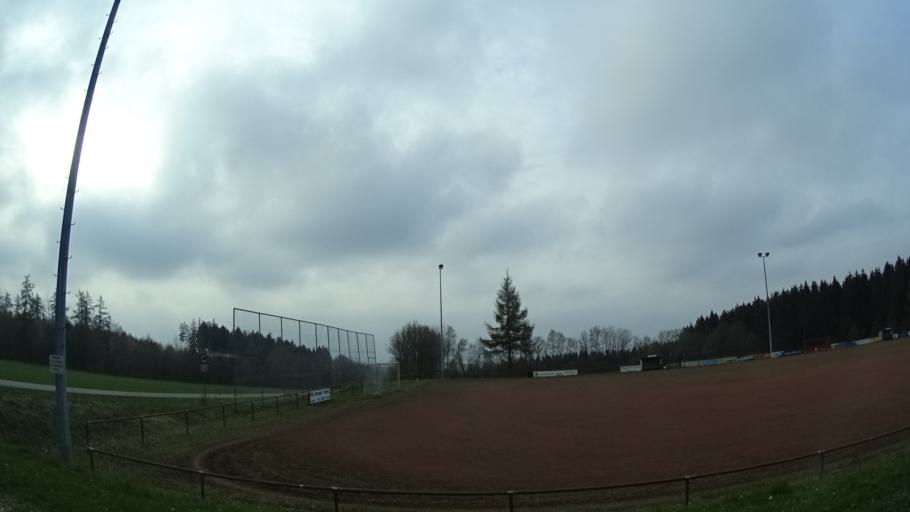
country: DE
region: Rheinland-Pfalz
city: Leisel
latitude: 49.7296
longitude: 7.1951
